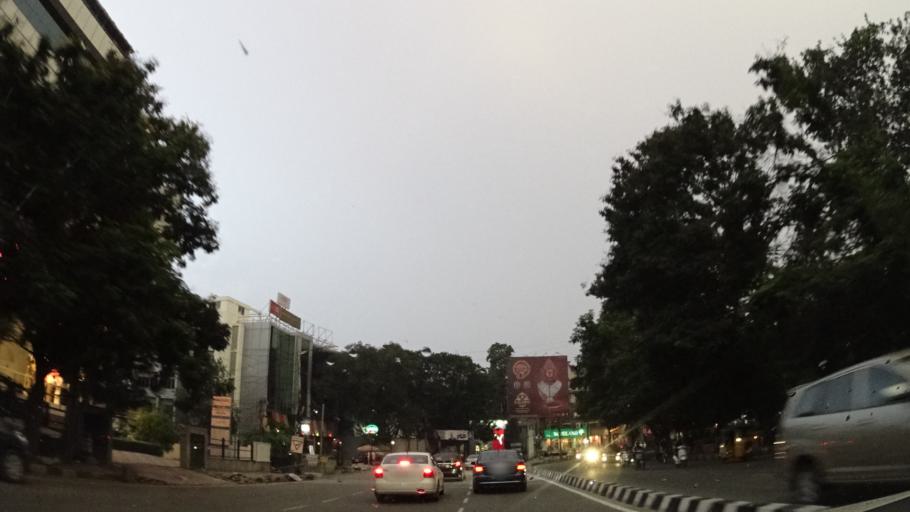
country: IN
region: Telangana
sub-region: Hyderabad
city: Hyderabad
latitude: 17.4231
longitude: 78.4490
